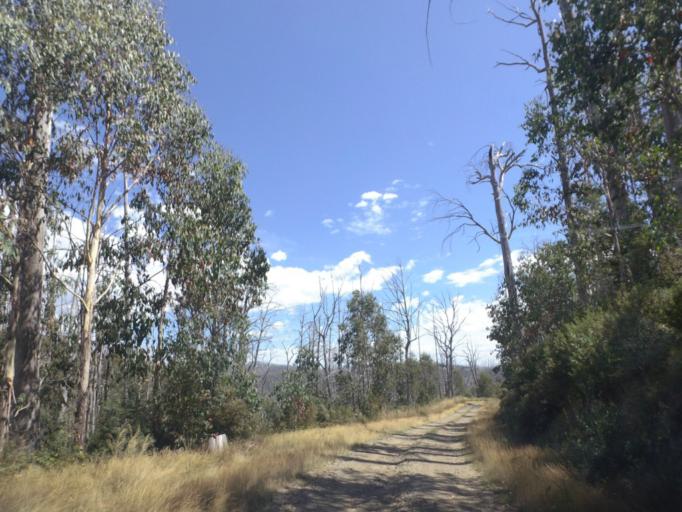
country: AU
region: Victoria
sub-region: Murrindindi
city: Alexandra
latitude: -37.4651
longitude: 145.8277
